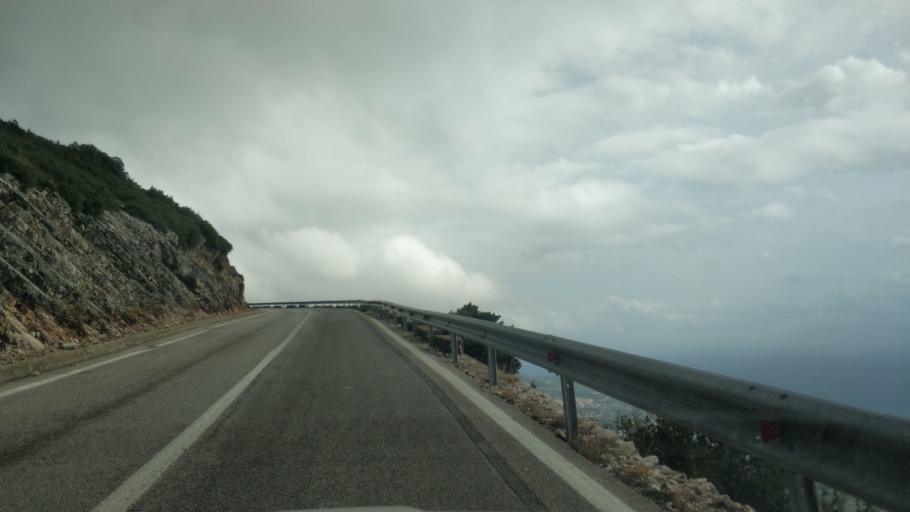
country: AL
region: Vlore
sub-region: Rrethi i Vlores
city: Vranisht
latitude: 40.1841
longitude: 19.5970
